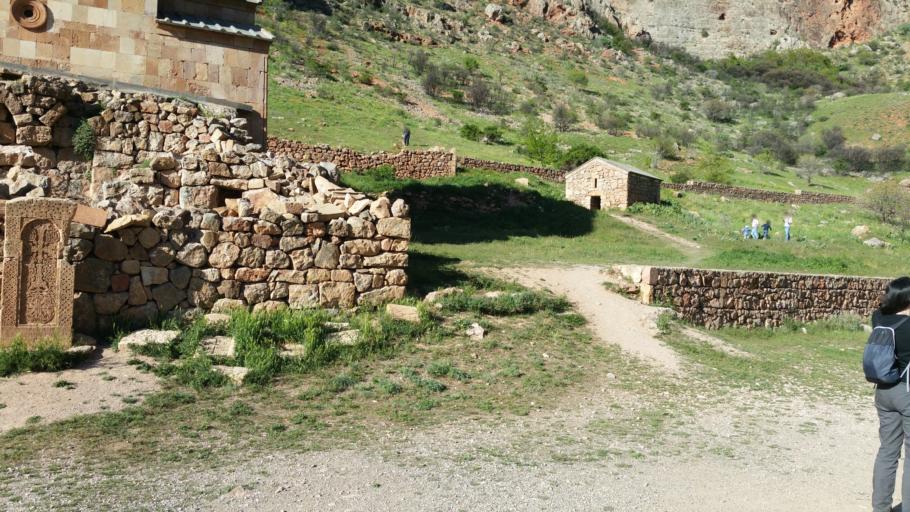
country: AM
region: Vayots' Dzori Marz
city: Areni
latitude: 39.6846
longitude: 45.2329
